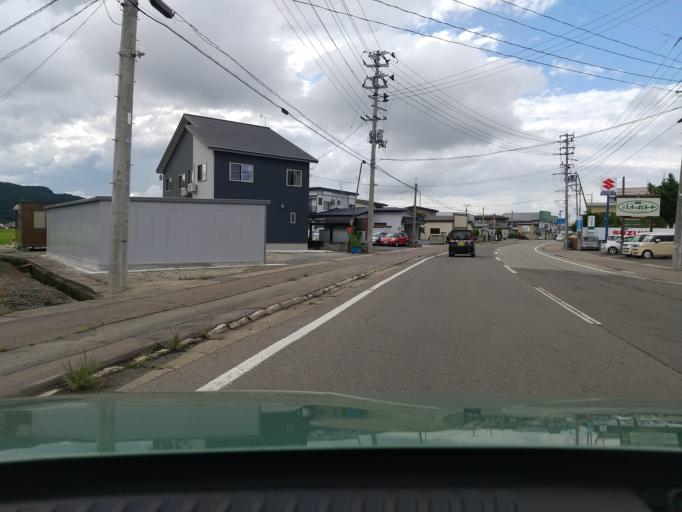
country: JP
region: Akita
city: Yuzawa
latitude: 39.1987
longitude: 140.5422
